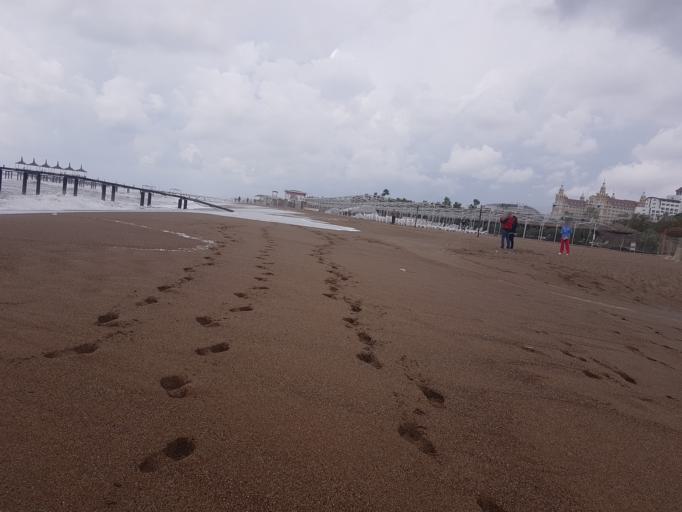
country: TR
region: Antalya
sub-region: Serik
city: Kumkoey
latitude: 36.8535
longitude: 30.8969
